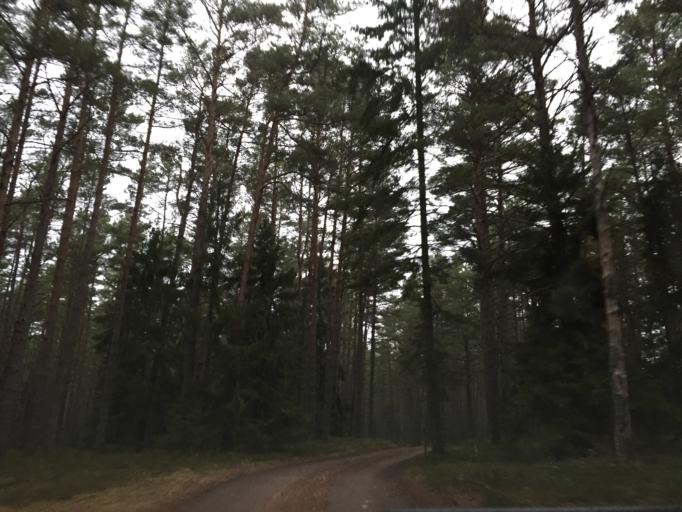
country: EE
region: Saare
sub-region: Kuressaare linn
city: Kuressaare
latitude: 58.5899
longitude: 22.5109
